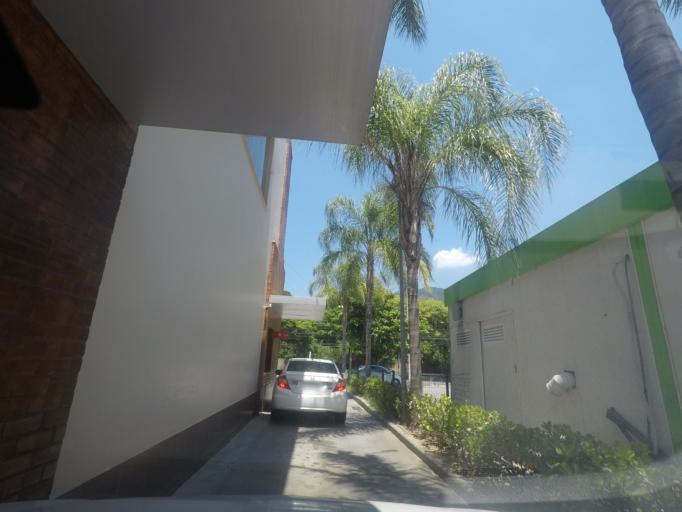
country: BR
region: Rio de Janeiro
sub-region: Nilopolis
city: Nilopolis
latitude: -22.9745
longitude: -43.4141
